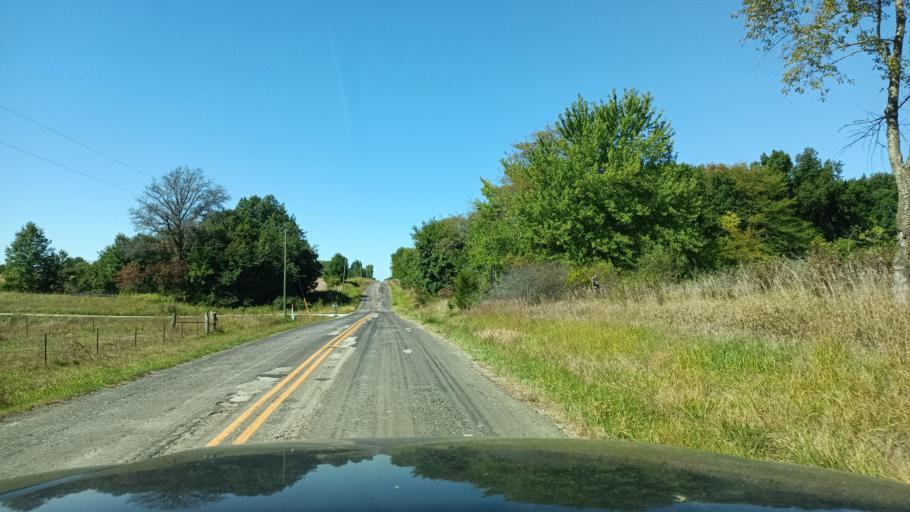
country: US
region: Missouri
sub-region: Scotland County
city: Memphis
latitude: 40.3549
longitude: -92.2202
